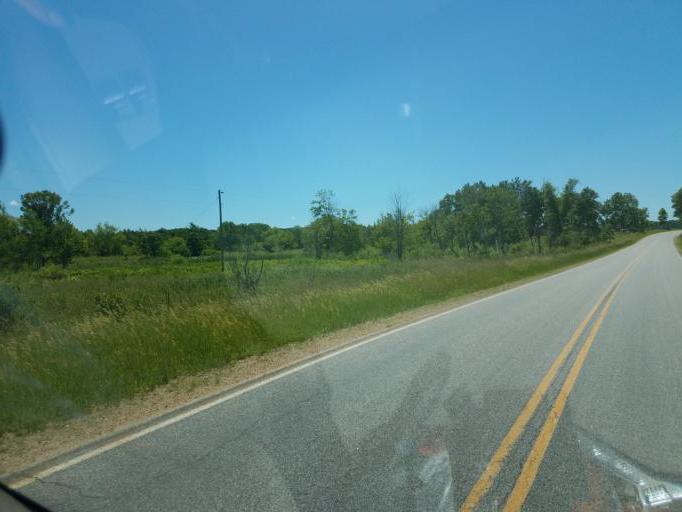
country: US
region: Wisconsin
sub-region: Juneau County
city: New Lisbon
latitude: 43.8688
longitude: -90.2771
